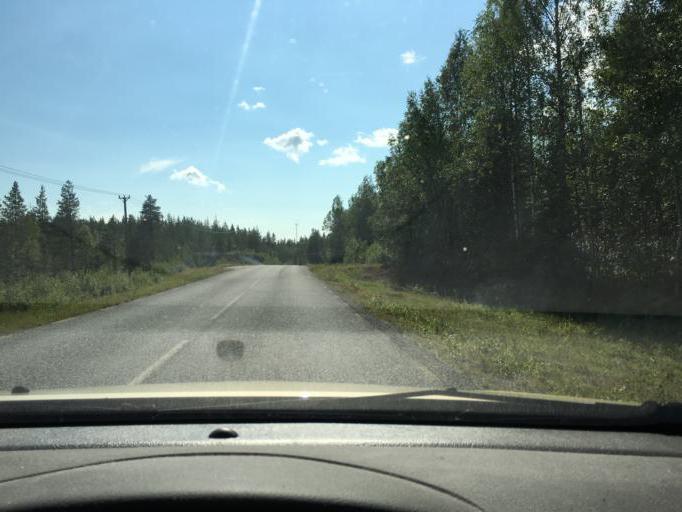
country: SE
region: Norrbotten
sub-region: Kalix Kommun
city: Toere
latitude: 66.0573
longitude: 22.5964
